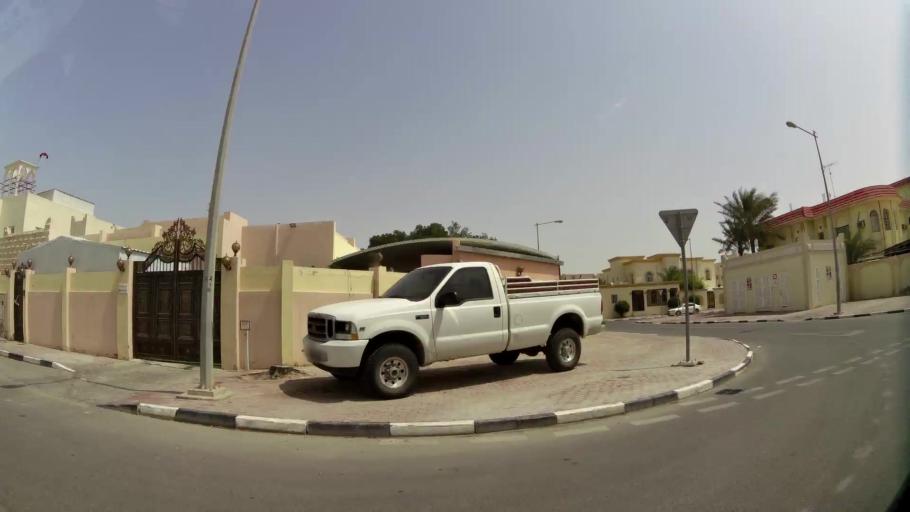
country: QA
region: Baladiyat ar Rayyan
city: Ar Rayyan
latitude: 25.2484
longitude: 51.4272
